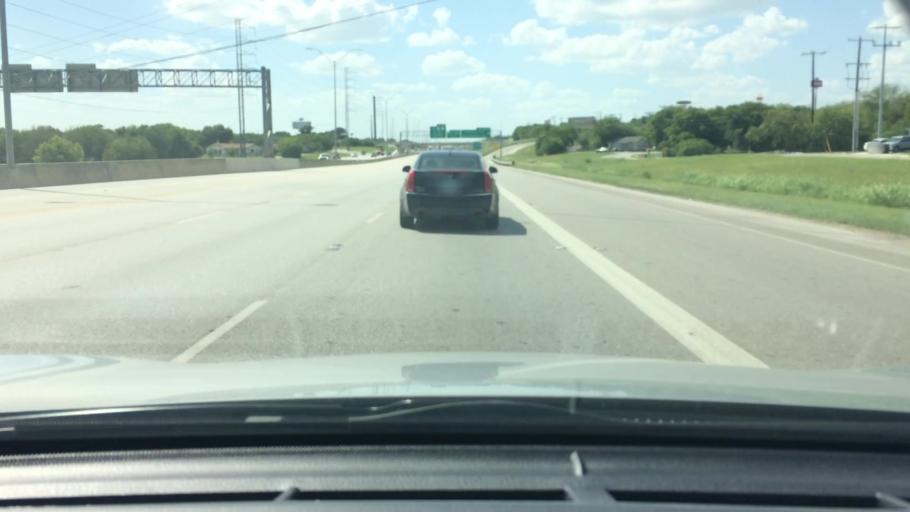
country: US
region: Texas
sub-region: Bexar County
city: San Antonio
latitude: 29.3707
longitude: -98.4535
